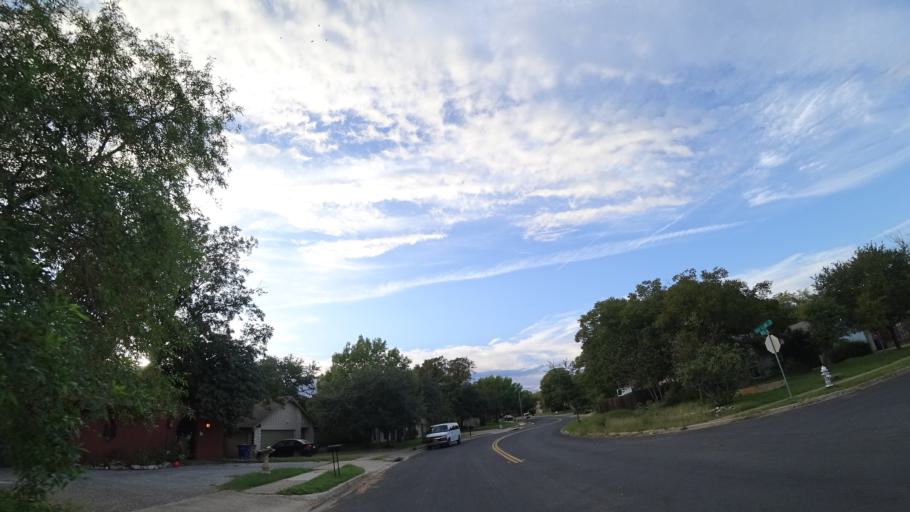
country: US
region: Texas
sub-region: Travis County
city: Austin
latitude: 30.2039
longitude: -97.7658
